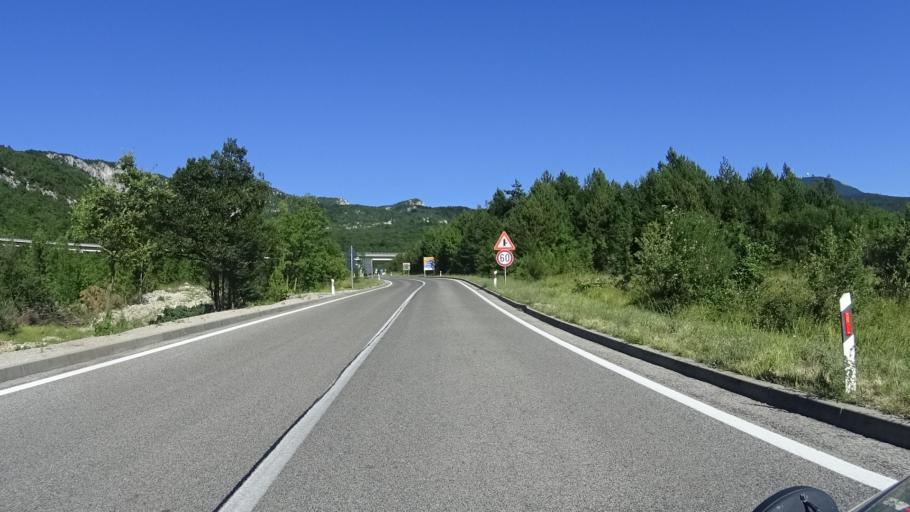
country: HR
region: Istarska
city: Lovran
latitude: 45.3204
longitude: 14.1681
